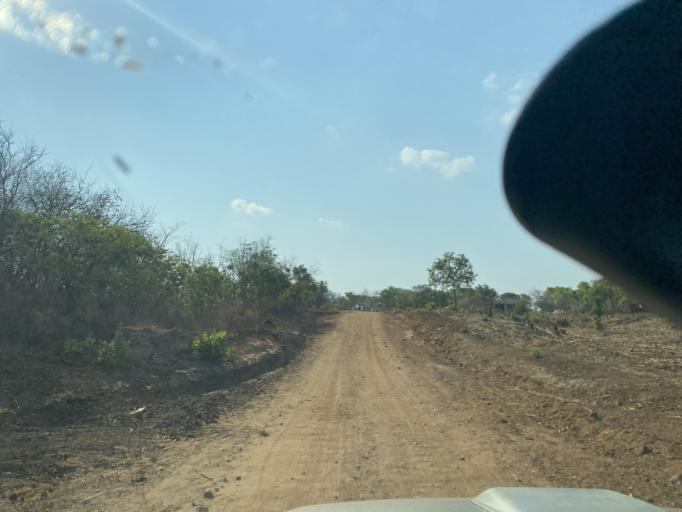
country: ZM
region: Lusaka
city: Chongwe
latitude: -15.3170
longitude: 28.7148
